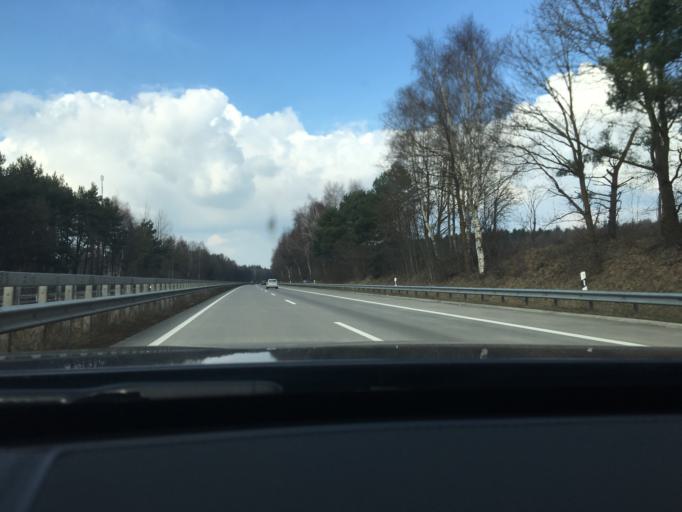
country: DE
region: Lower Saxony
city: Wulsbuttel
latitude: 53.2885
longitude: 8.6266
